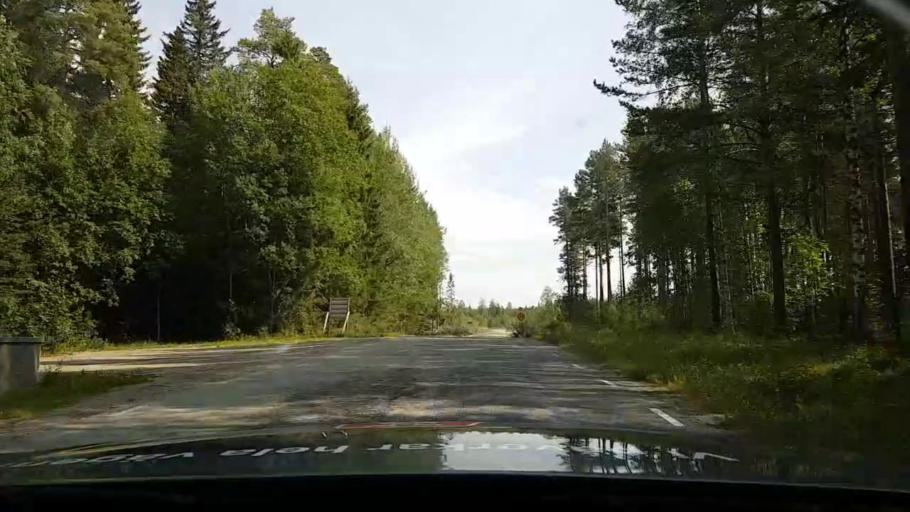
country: SE
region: Jaemtland
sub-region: Braecke Kommun
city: Braecke
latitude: 62.7412
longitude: 15.4352
